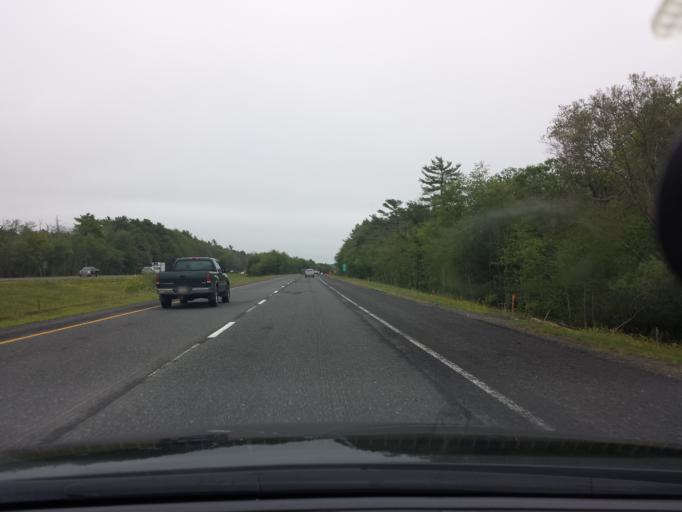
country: US
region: Massachusetts
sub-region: Plymouth County
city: Mattapoisett
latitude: 41.6629
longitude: -70.8562
